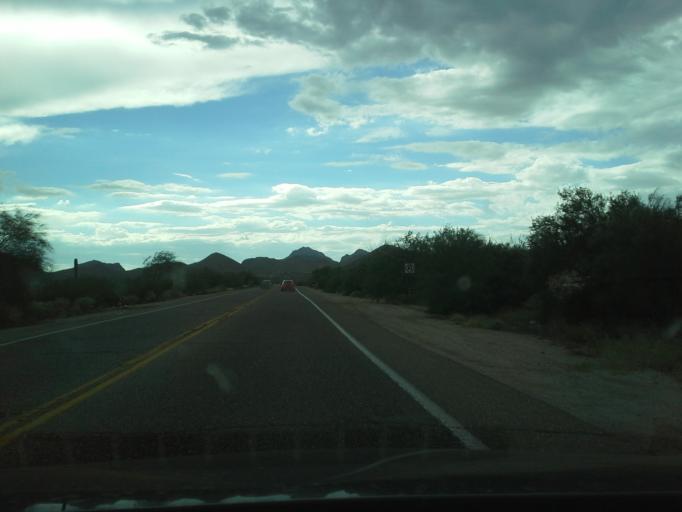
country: US
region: Arizona
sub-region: Pima County
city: South Tucson
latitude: 32.2070
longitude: -111.0027
